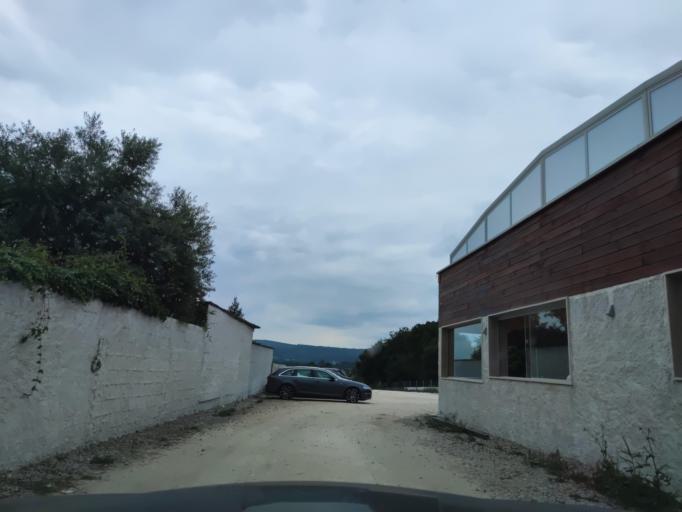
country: ES
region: Galicia
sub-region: Provincia da Coruna
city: Teo
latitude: 42.7975
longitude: -8.5340
